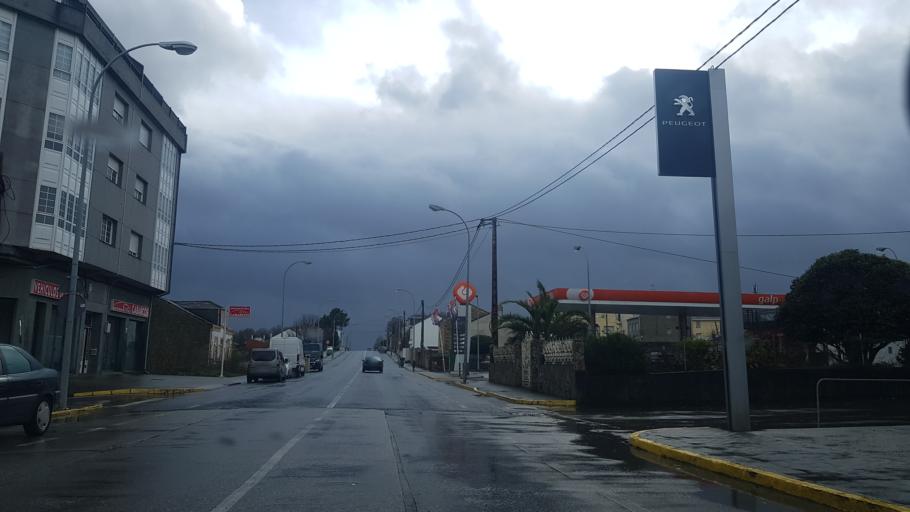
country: ES
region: Galicia
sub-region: Provincia de Lugo
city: Vilalba
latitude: 43.2894
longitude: -7.6791
